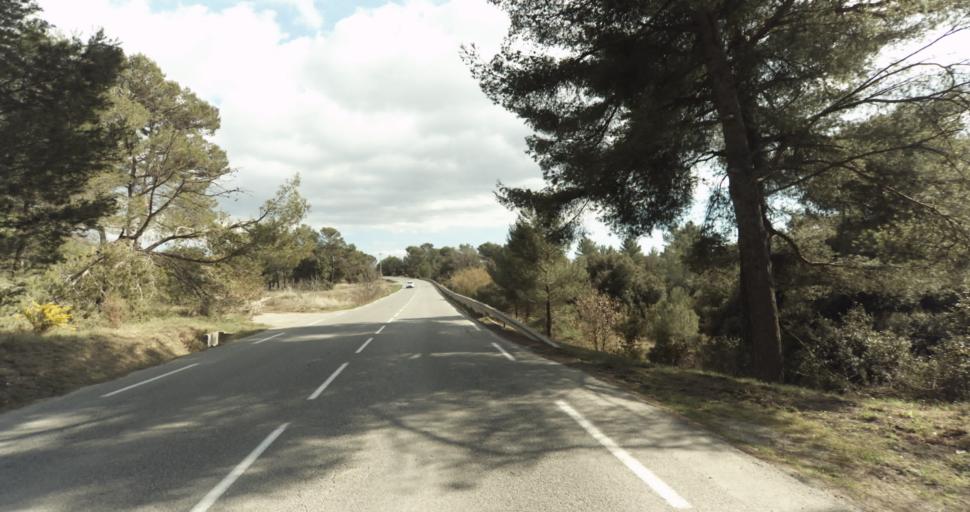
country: FR
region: Provence-Alpes-Cote d'Azur
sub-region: Departement des Bouches-du-Rhone
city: Greasque
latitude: 43.4449
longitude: 5.5244
